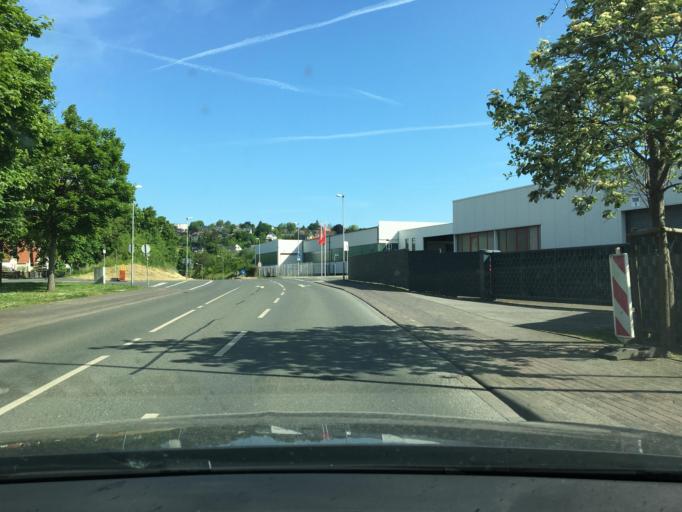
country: DE
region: North Rhine-Westphalia
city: Wickede
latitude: 51.4887
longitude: 7.8588
